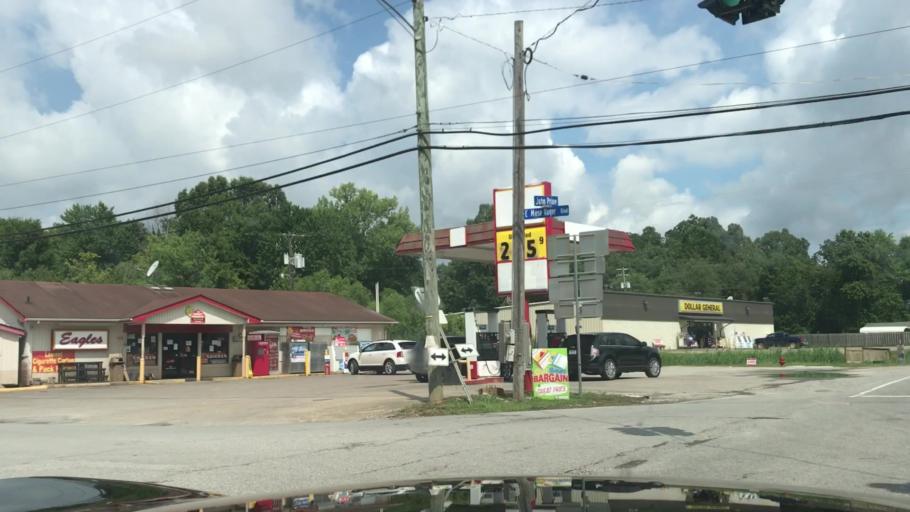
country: US
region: Kentucky
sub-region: Muhlenberg County
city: Central City
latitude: 37.2188
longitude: -87.0459
